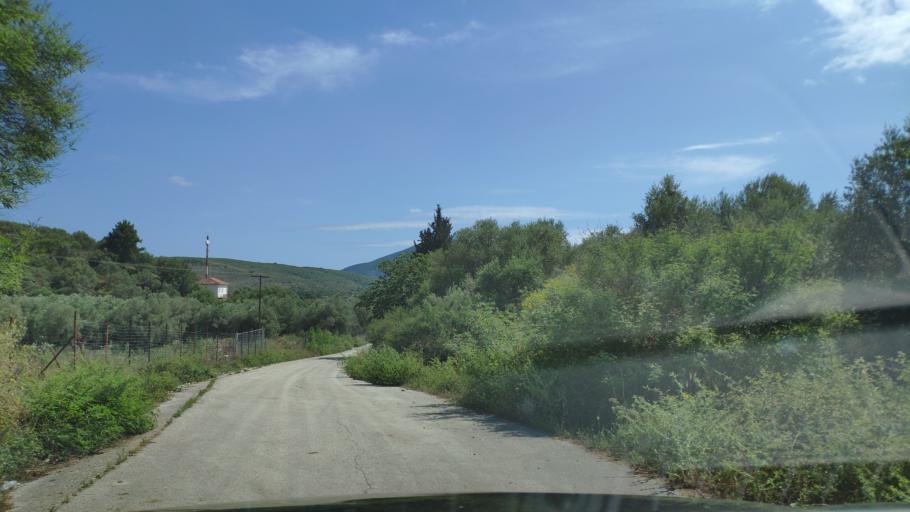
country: AL
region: Vlore
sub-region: Rrethi i Sarandes
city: Konispol
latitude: 39.6225
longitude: 20.2010
